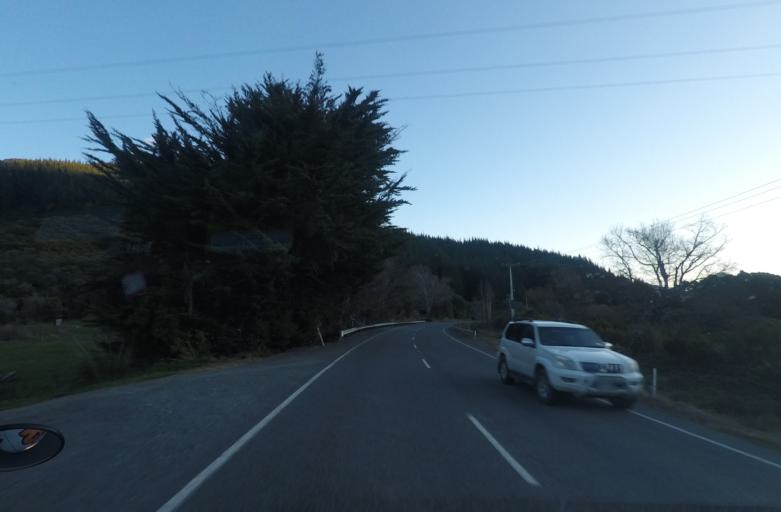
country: NZ
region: Marlborough
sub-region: Marlborough District
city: Picton
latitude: -41.2823
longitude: 173.7263
